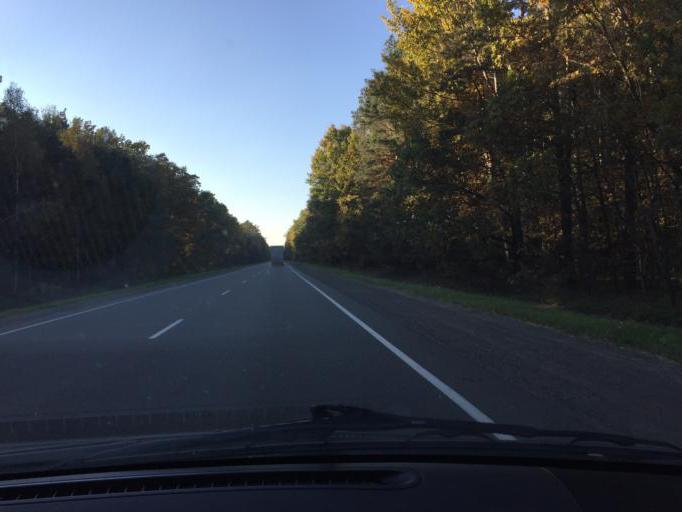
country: BY
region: Brest
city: Horad Luninyets
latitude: 52.2834
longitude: 26.8122
